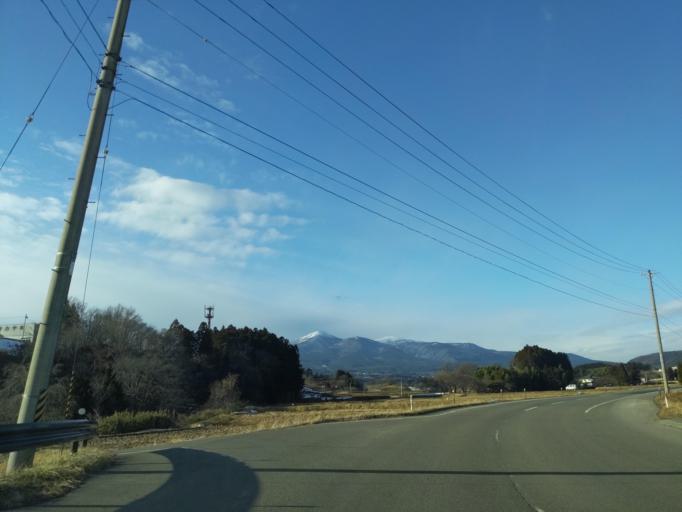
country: JP
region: Fukushima
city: Motomiya
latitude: 37.5285
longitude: 140.3628
